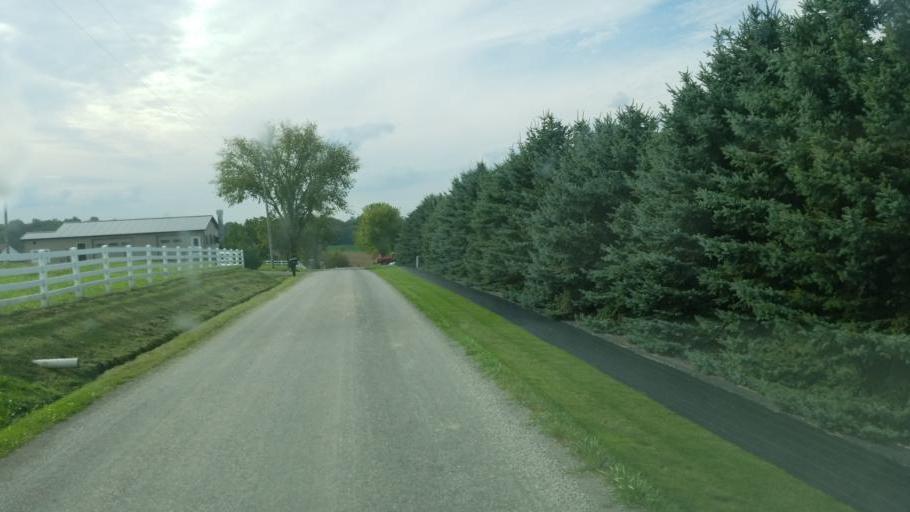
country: US
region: Ohio
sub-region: Holmes County
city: Millersburg
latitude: 40.6075
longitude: -81.7979
